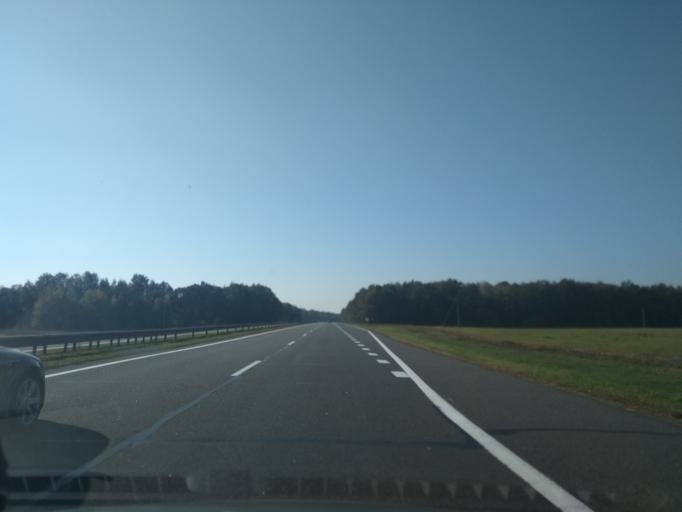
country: BY
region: Brest
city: Ivatsevichy
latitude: 52.7243
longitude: 25.4366
